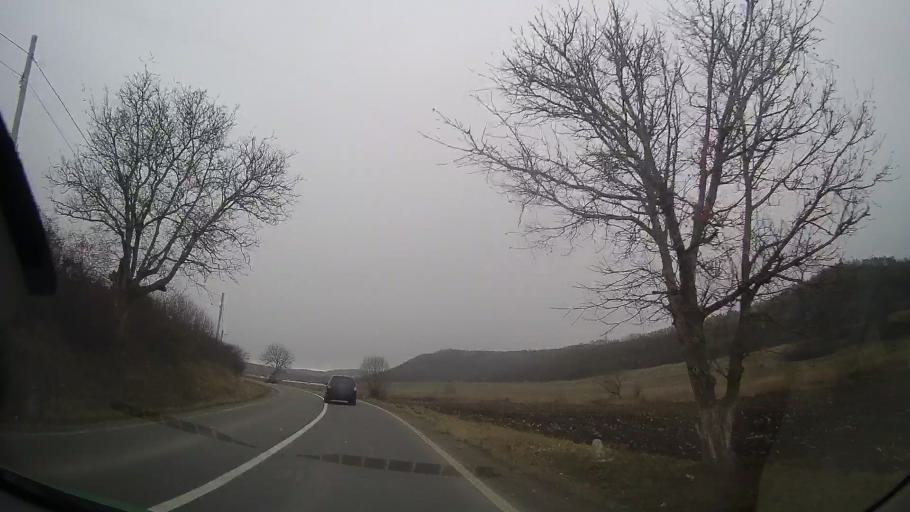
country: RO
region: Mures
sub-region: Comuna Ceausu de Campie
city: Ceausu de Campie
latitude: 46.6253
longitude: 24.5218
